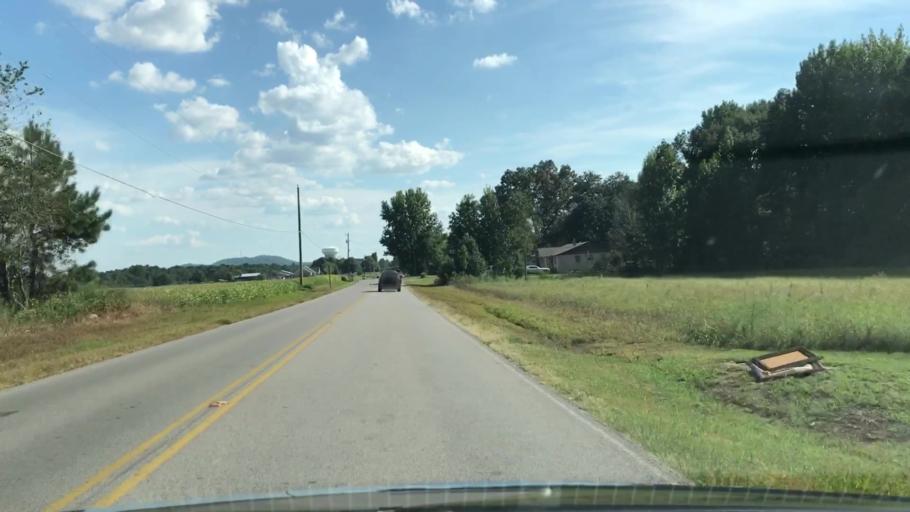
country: US
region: Alabama
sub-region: Madison County
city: Harvest
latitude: 34.8737
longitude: -86.7489
